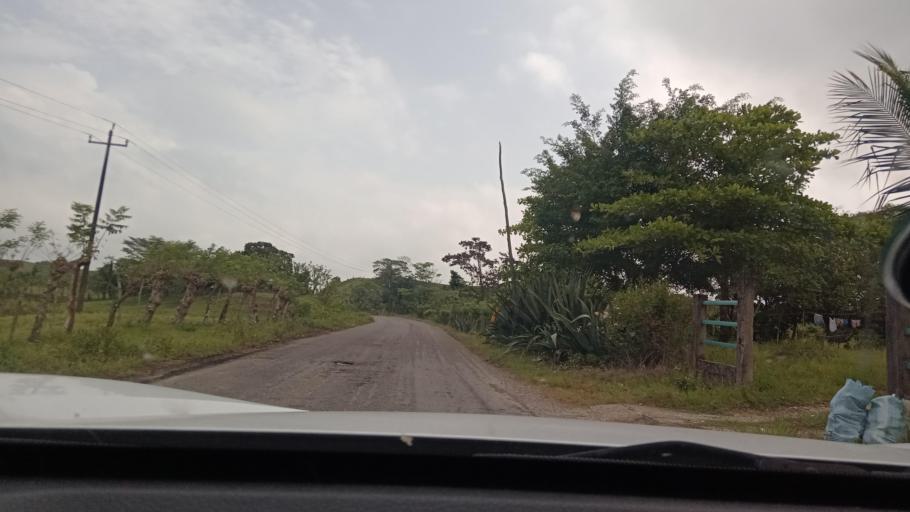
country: MX
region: Tabasco
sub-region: Huimanguillo
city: Francisco Rueda
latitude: 17.5475
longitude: -94.1275
